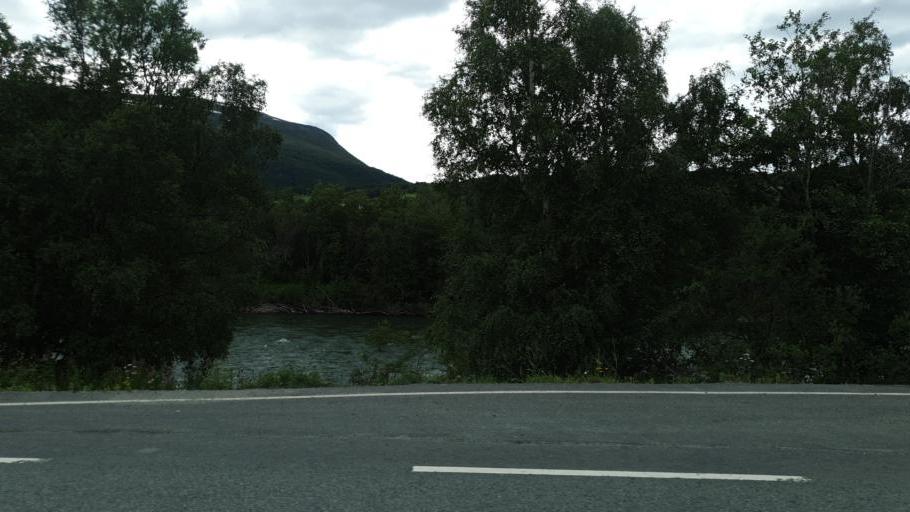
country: NO
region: Sor-Trondelag
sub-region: Oppdal
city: Oppdal
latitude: 62.5562
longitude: 9.6349
